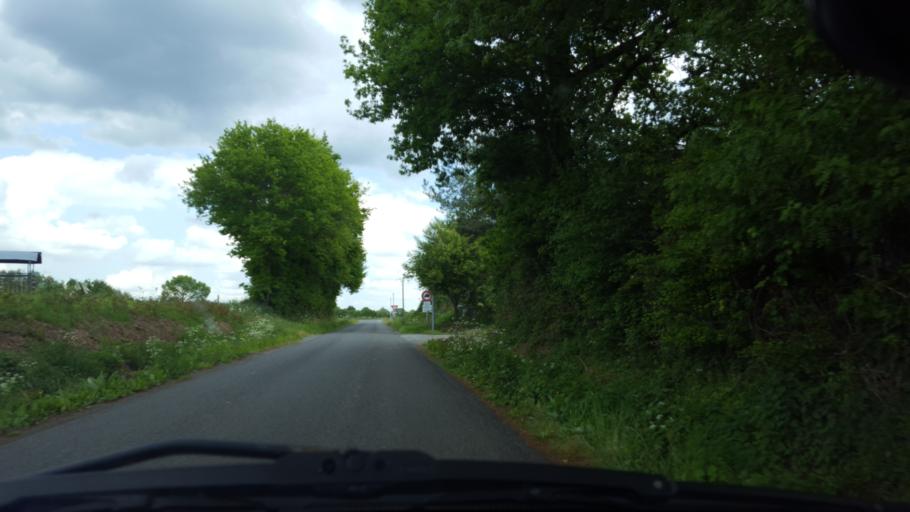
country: FR
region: Pays de la Loire
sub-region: Departement de la Loire-Atlantique
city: Saint-Philbert-de-Grand-Lieu
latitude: 47.0378
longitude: -1.6018
